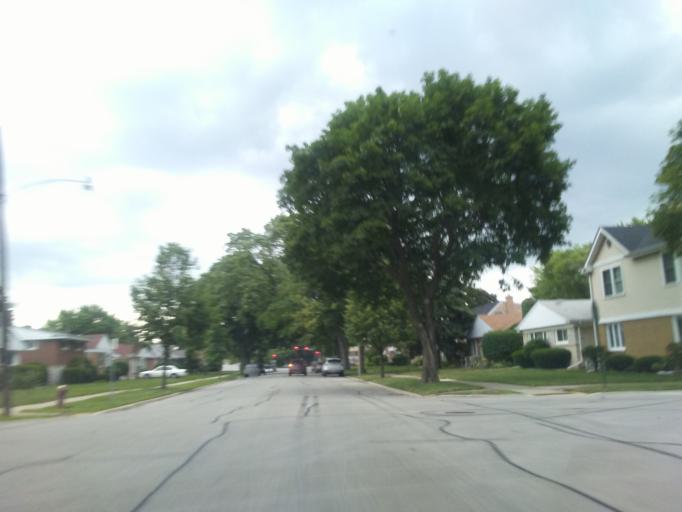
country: US
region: Illinois
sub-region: Cook County
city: Skokie
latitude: 42.0244
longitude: -87.7379
